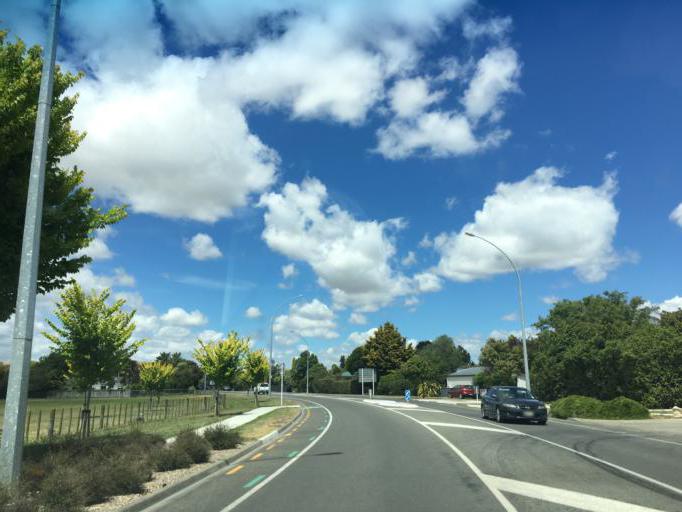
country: NZ
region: Hawke's Bay
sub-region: Hastings District
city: Hastings
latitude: -39.6593
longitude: 176.8857
